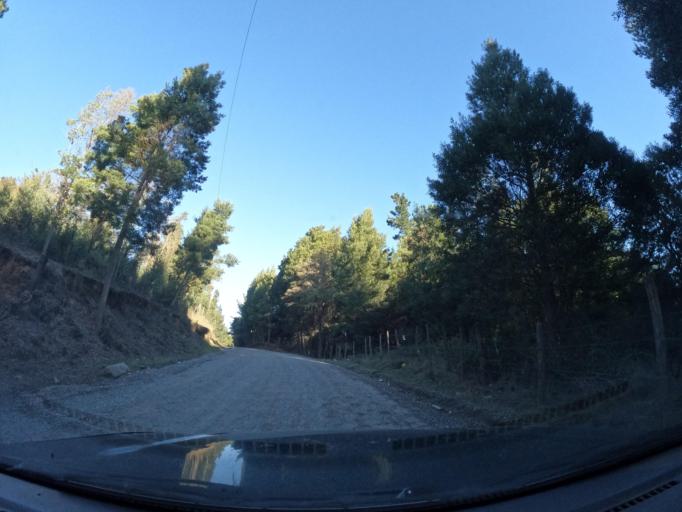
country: CL
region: Biobio
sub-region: Provincia de Concepcion
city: Chiguayante
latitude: -37.0194
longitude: -72.8917
